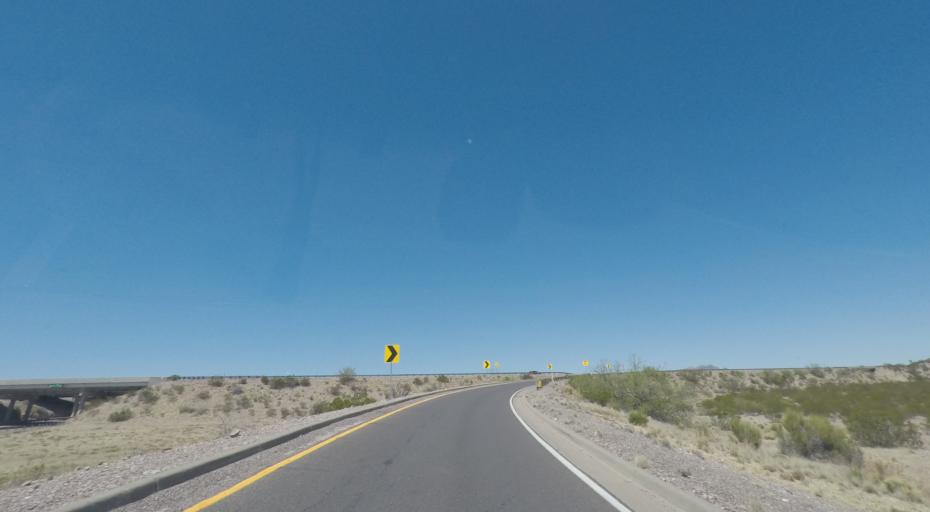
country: US
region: New Mexico
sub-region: Socorro County
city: Socorro
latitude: 33.9180
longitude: -106.8776
